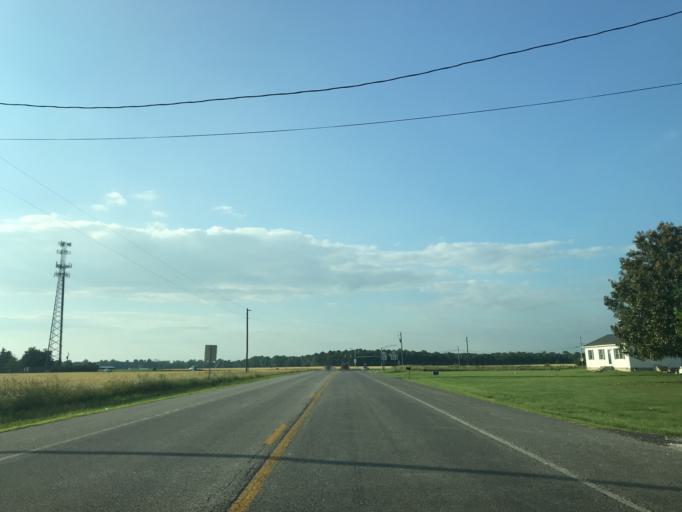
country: US
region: Maryland
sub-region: Caroline County
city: Denton
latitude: 38.8338
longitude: -75.7783
